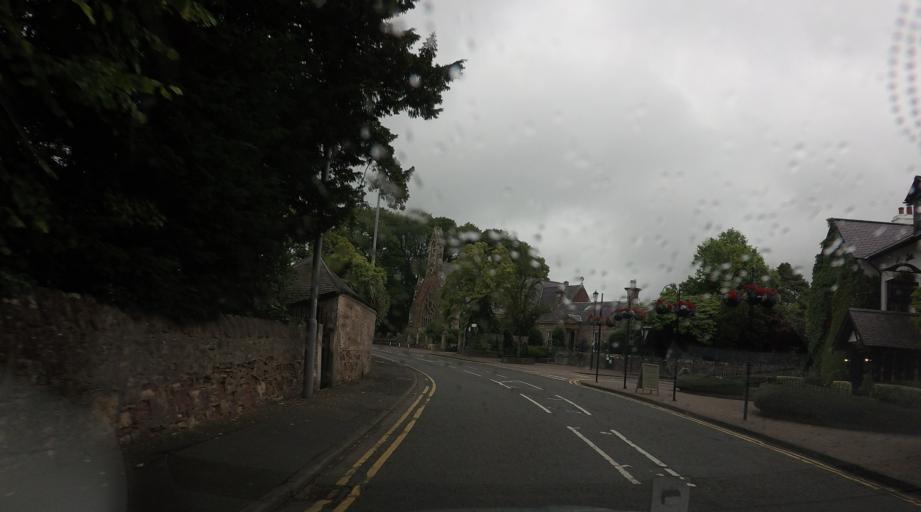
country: GB
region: Scotland
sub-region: South Ayrshire
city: Ayr
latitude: 55.4272
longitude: -4.6376
